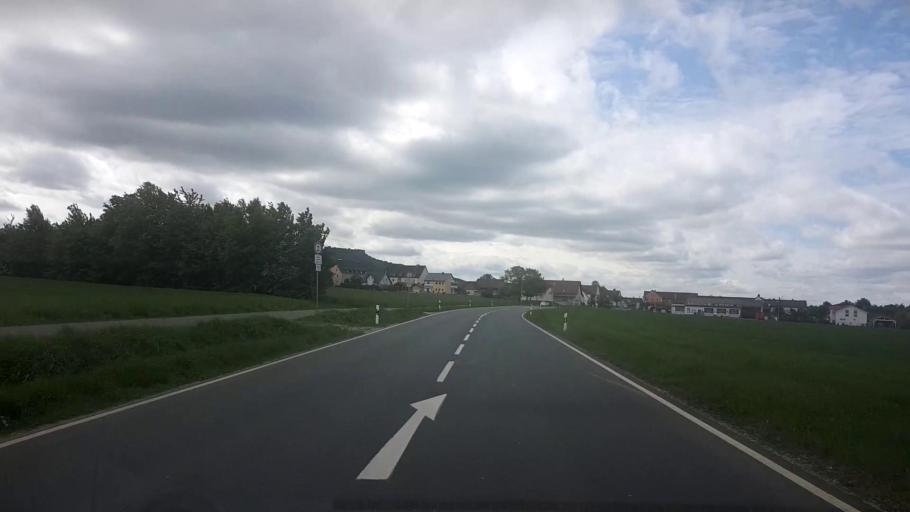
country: DE
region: Bavaria
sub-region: Upper Franconia
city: Lichtenfels
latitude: 50.1260
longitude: 11.0385
